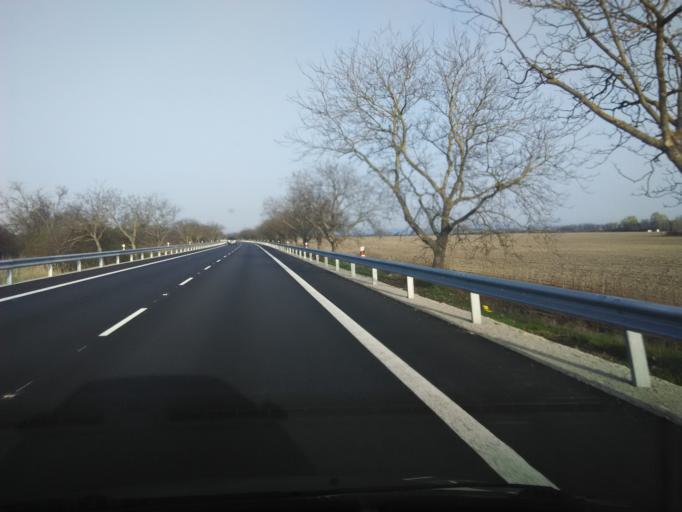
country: SK
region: Trnavsky
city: Sladkovicovo
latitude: 48.1958
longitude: 17.5869
